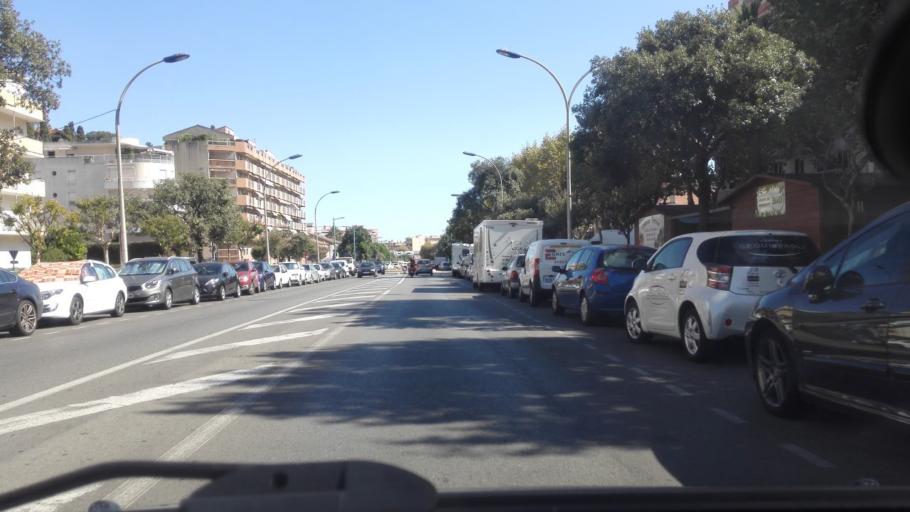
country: FR
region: Provence-Alpes-Cote d'Azur
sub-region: Departement des Alpes-Maritimes
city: Roquebrune-Cap-Martin
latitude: 43.7765
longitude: 7.4878
